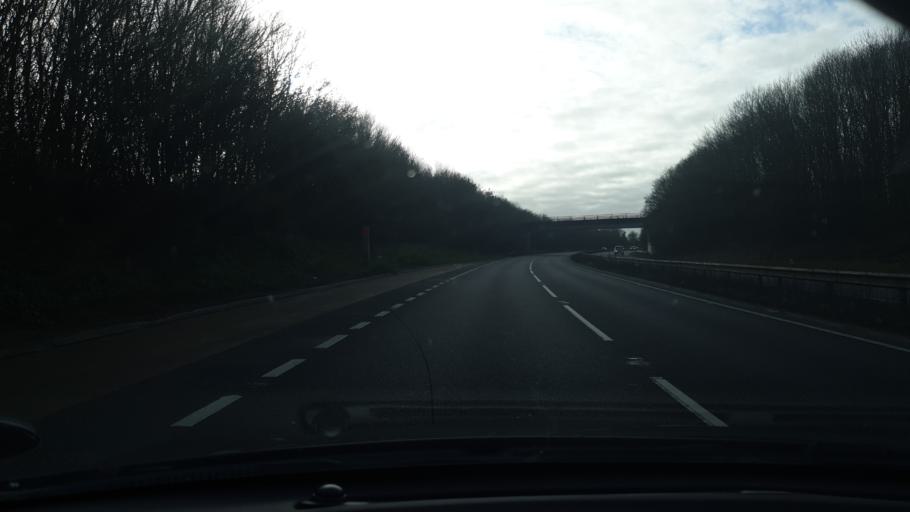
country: GB
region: England
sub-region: Suffolk
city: Bramford
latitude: 52.0300
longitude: 1.0949
